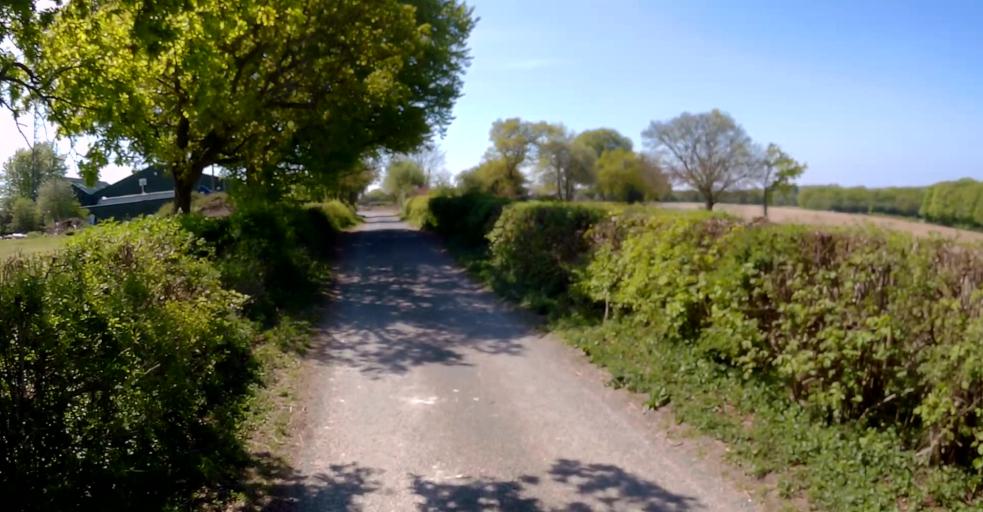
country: GB
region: England
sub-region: Hampshire
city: Overton
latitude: 51.1945
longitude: -1.2465
